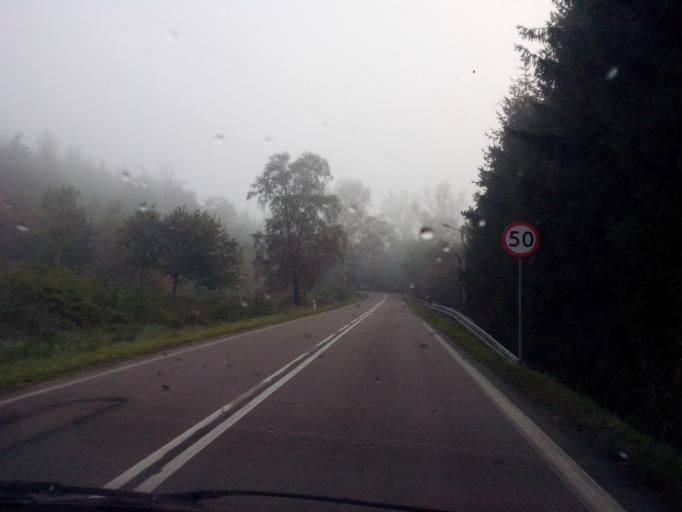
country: PL
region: Subcarpathian Voivodeship
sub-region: Powiat brzozowski
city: Domaradz
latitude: 49.7963
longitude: 21.9504
